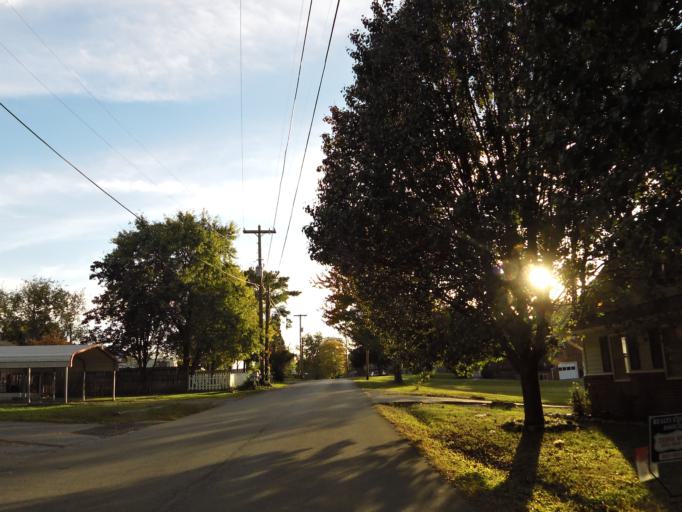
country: US
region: Tennessee
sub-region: Blount County
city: Eagleton Village
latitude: 35.7914
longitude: -83.9482
